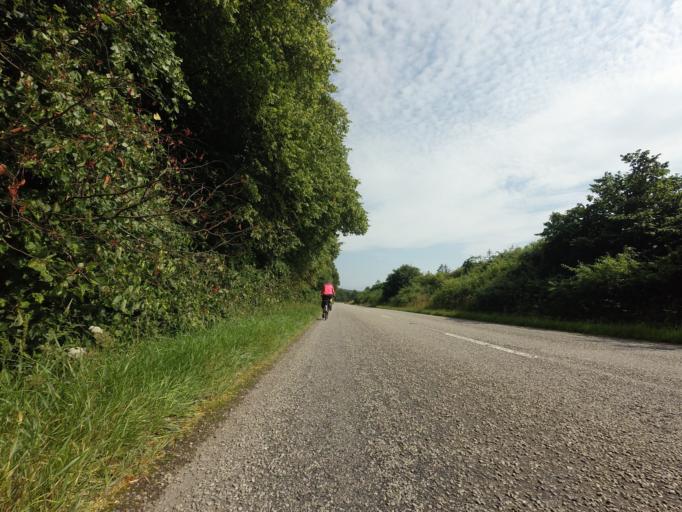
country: GB
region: Scotland
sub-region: Highland
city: Alness
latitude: 57.9126
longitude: -4.3778
